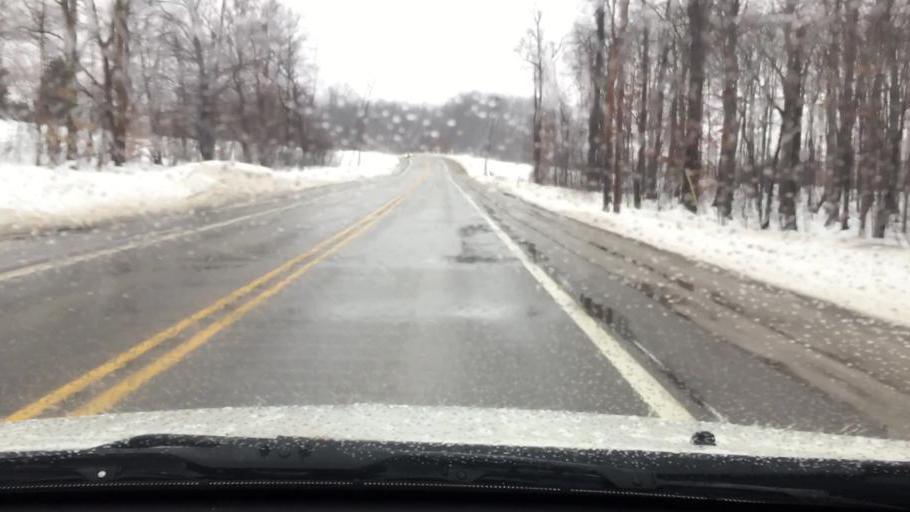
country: US
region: Michigan
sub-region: Charlevoix County
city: East Jordan
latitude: 45.2059
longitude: -85.1655
